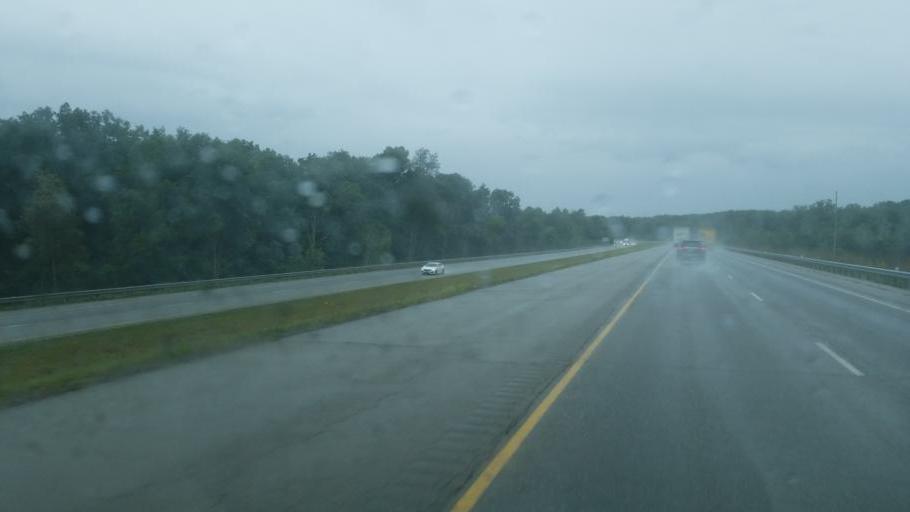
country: US
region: Ohio
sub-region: Summit County
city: Peninsula
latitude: 41.2551
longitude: -81.5759
